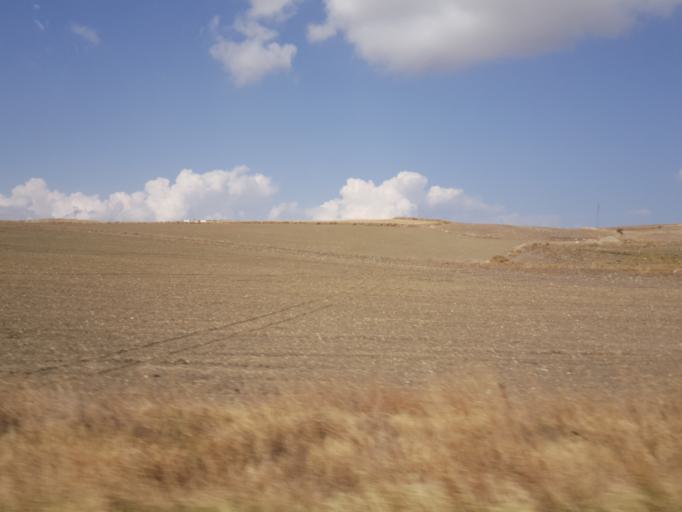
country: TR
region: Corum
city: Bogazkale
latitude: 40.1542
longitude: 34.6004
